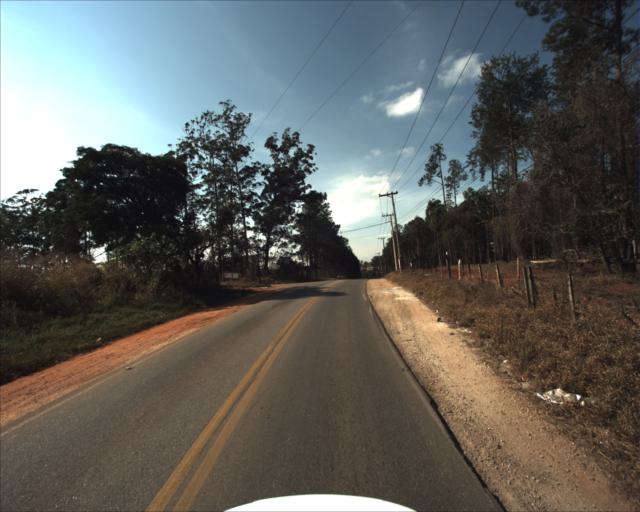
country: BR
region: Sao Paulo
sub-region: Sorocaba
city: Sorocaba
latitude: -23.4415
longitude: -47.5290
